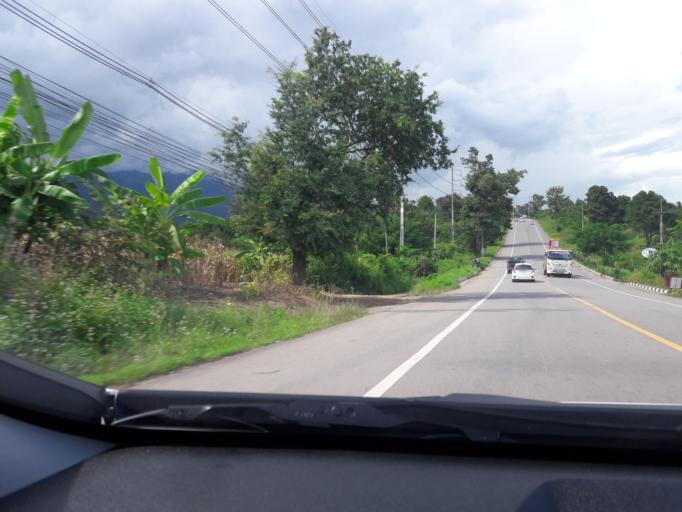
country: TH
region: Mae Hong Son
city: Mae Hi
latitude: 19.3310
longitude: 98.4339
